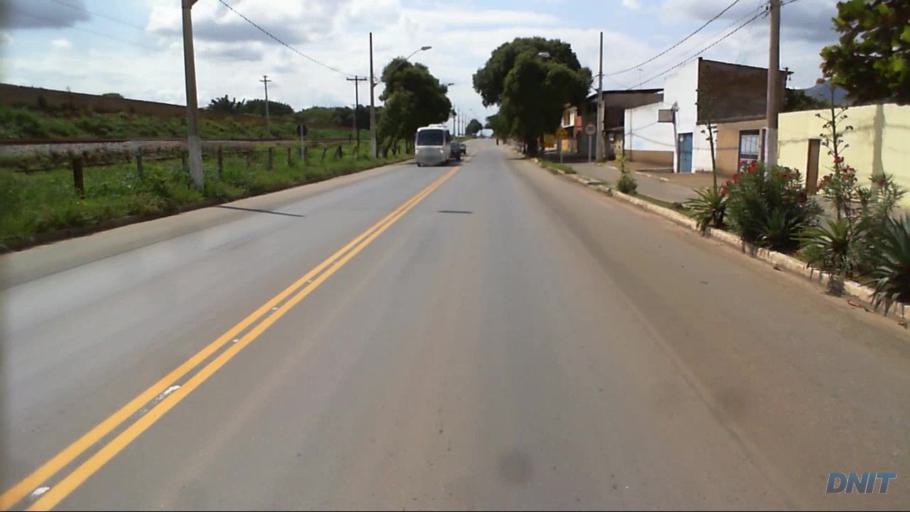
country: BR
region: Minas Gerais
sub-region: Governador Valadares
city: Governador Valadares
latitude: -18.9080
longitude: -41.9928
